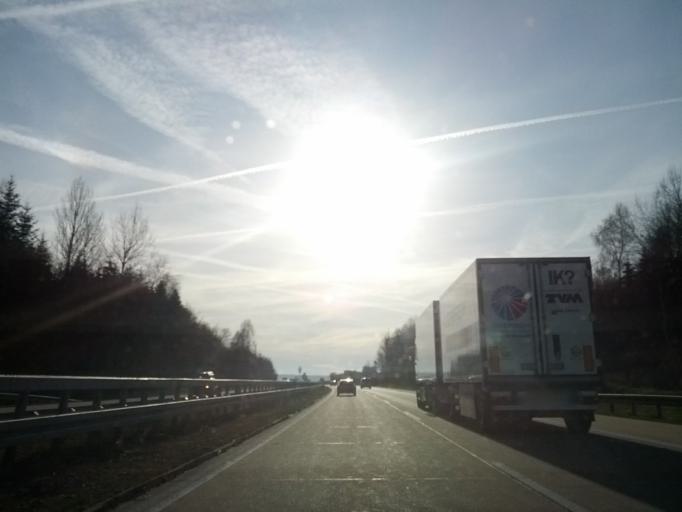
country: DE
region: Baden-Wuerttemberg
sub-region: Regierungsbezirk Stuttgart
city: Ellwangen
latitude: 48.9668
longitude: 10.1854
